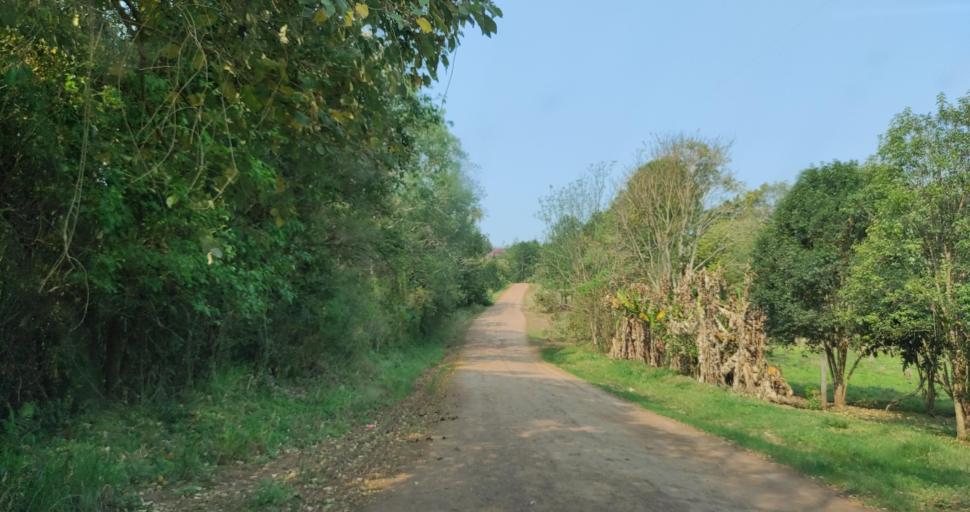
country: AR
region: Misiones
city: Cerro Azul
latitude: -27.6262
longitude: -55.5344
